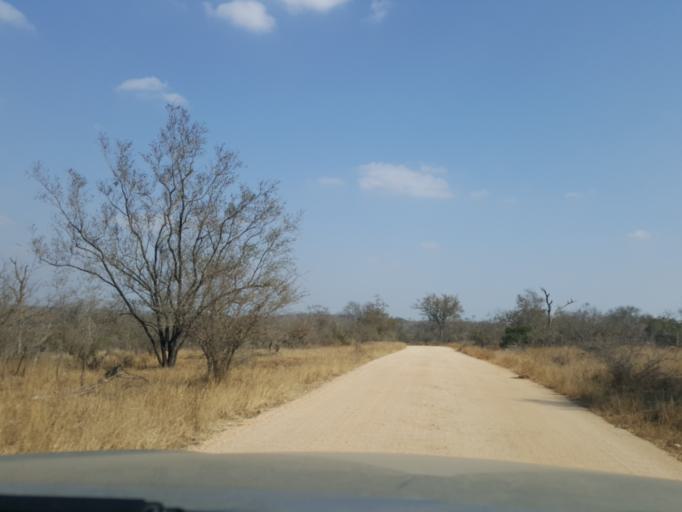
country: ZA
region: Mpumalanga
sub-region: Ehlanzeni District
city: Komatipoort
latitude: -25.2834
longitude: 31.7708
